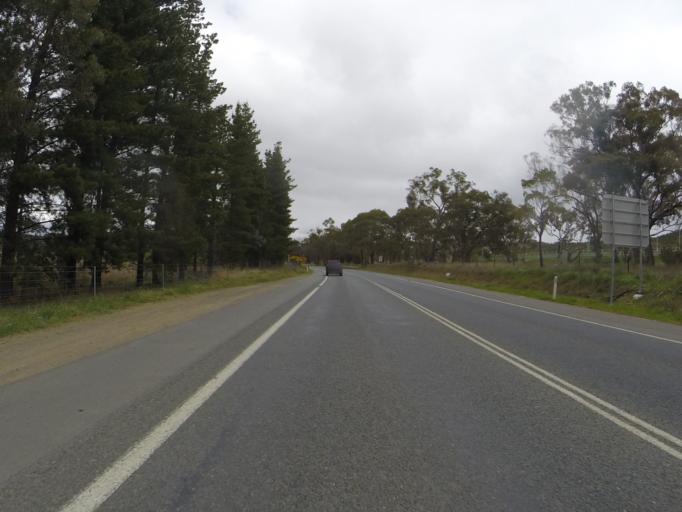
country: AU
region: Australian Capital Territory
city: Canberra
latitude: -35.2449
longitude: 149.1921
